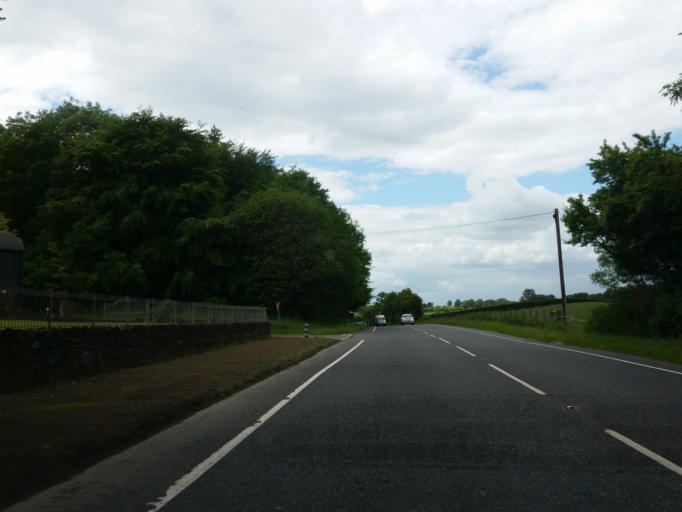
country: GB
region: Northern Ireland
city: Fivemiletown
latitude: 54.4037
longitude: -7.1940
